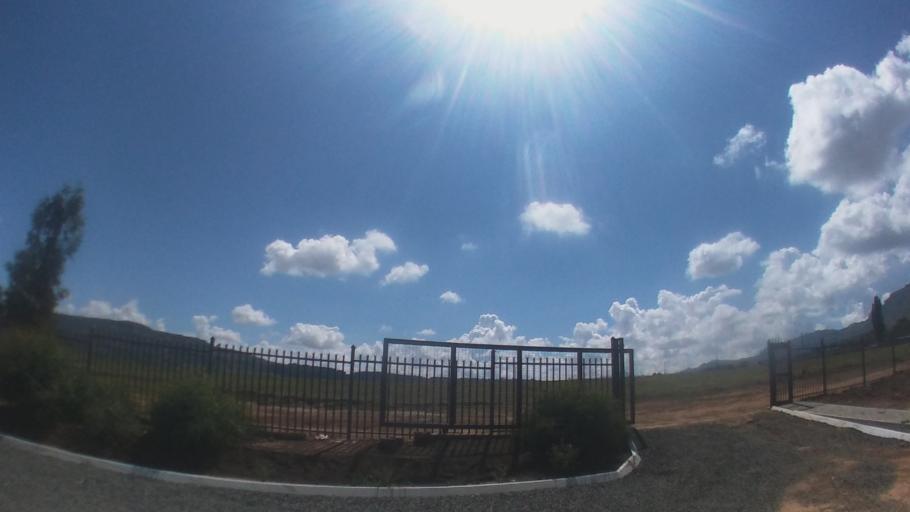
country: LS
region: Maseru
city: Nako
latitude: -29.6216
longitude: 27.4997
